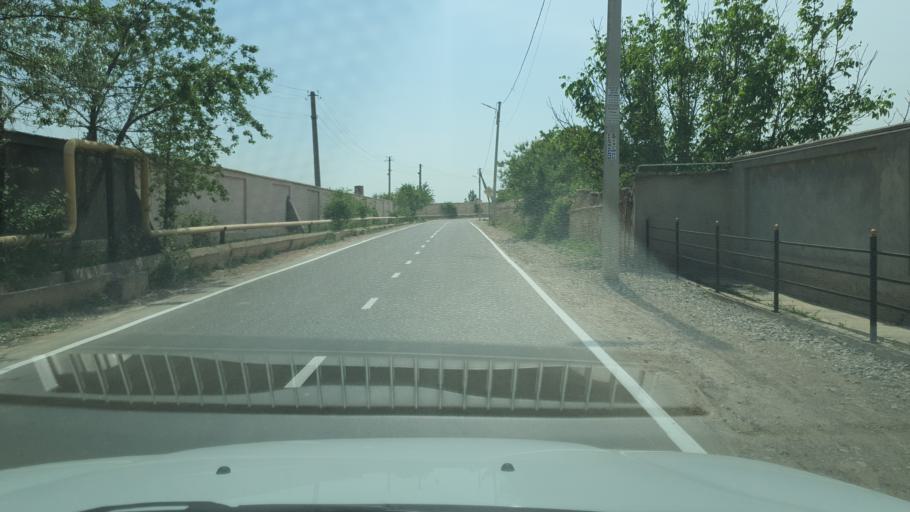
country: UZ
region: Toshkent
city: Salor
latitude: 41.4530
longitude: 69.4011
